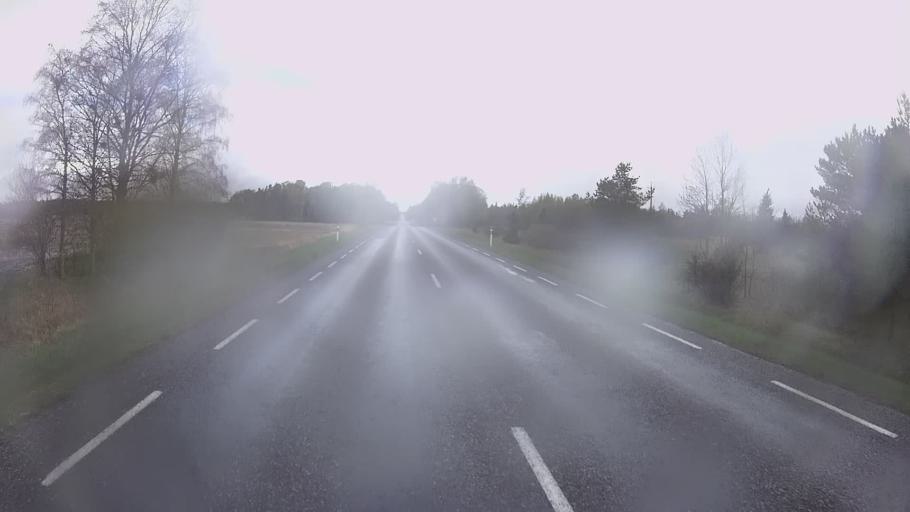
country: EE
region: Hiiumaa
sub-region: Kaerdla linn
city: Kardla
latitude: 58.9536
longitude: 22.8728
